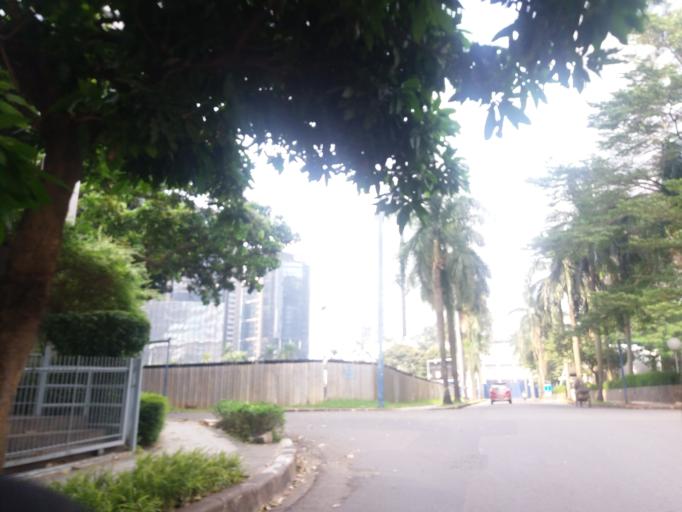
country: ID
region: Jakarta Raya
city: Jakarta
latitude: -6.2289
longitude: 106.8242
